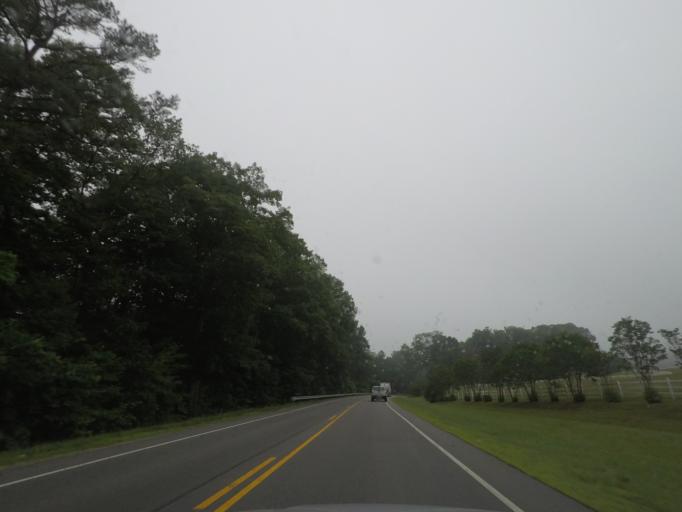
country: US
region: Virginia
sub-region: Buckingham County
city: Buckingham
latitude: 37.4638
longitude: -78.4690
